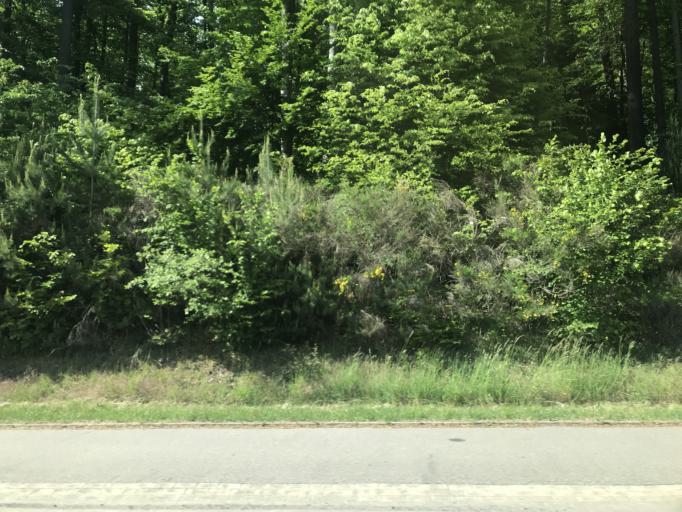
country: DE
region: Saarland
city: Losheim
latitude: 49.4505
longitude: 6.7544
